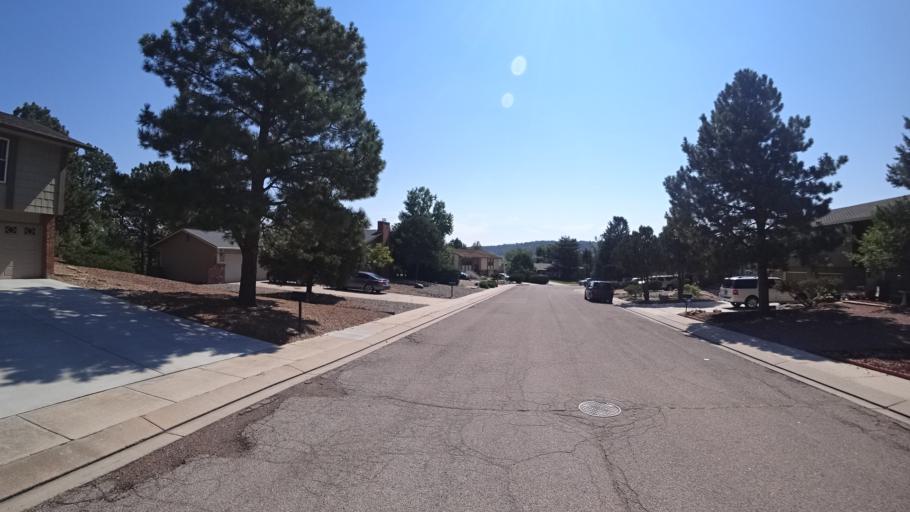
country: US
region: Colorado
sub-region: El Paso County
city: Air Force Academy
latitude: 38.9211
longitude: -104.8219
